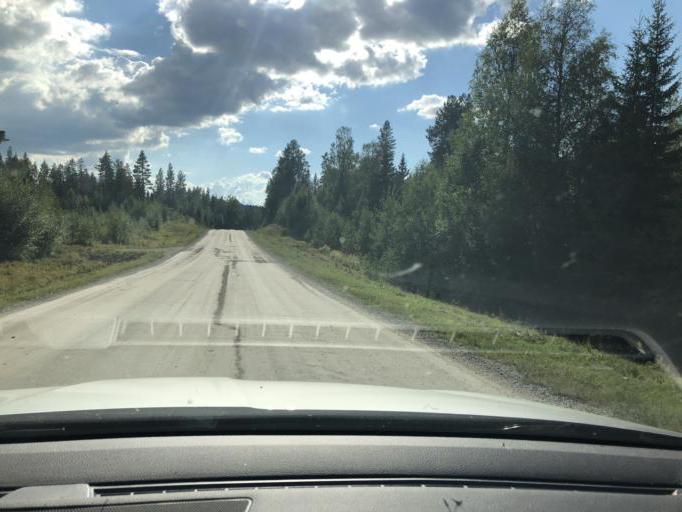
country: SE
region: Vaesternorrland
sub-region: Solleftea Kommun
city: Solleftea
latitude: 63.3160
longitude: 17.2288
